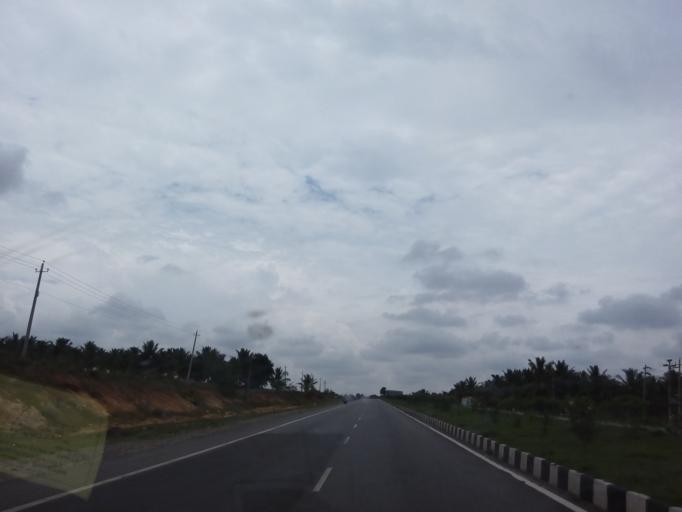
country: IN
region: Karnataka
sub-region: Hassan
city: Channarayapatna
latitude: 12.9759
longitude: 76.3016
